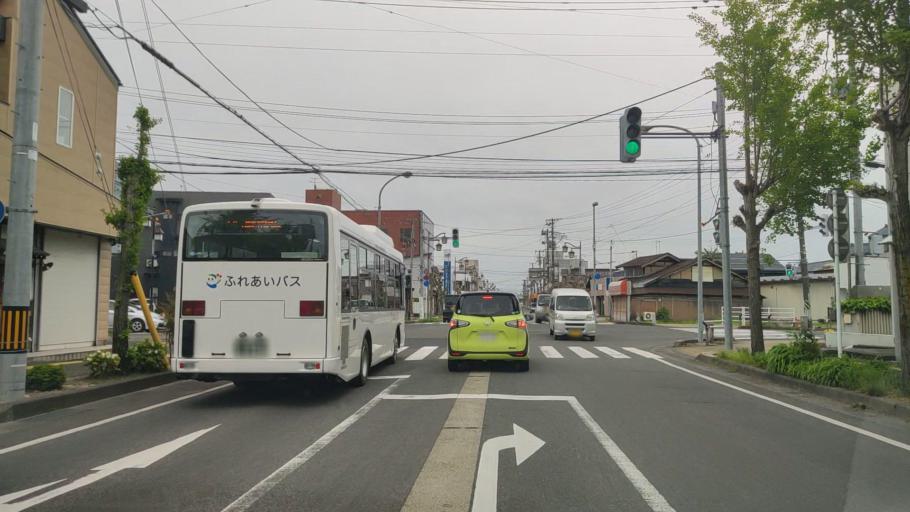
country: JP
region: Niigata
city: Gosen
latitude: 37.7382
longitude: 139.1805
